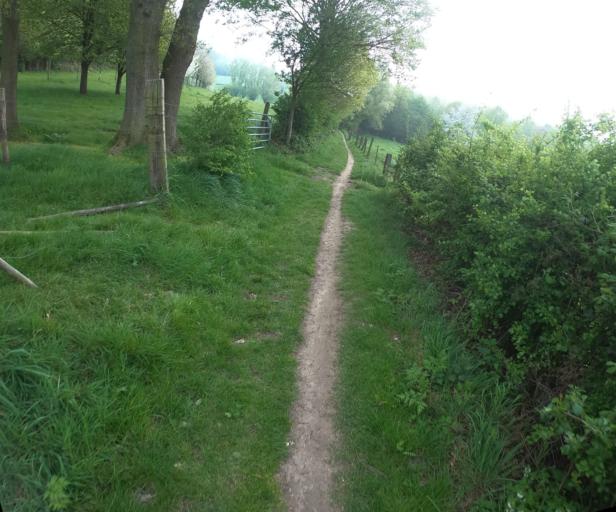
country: BE
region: Flanders
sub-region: Provincie Vlaams-Brabant
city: Gooik
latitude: 50.7810
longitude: 4.1047
